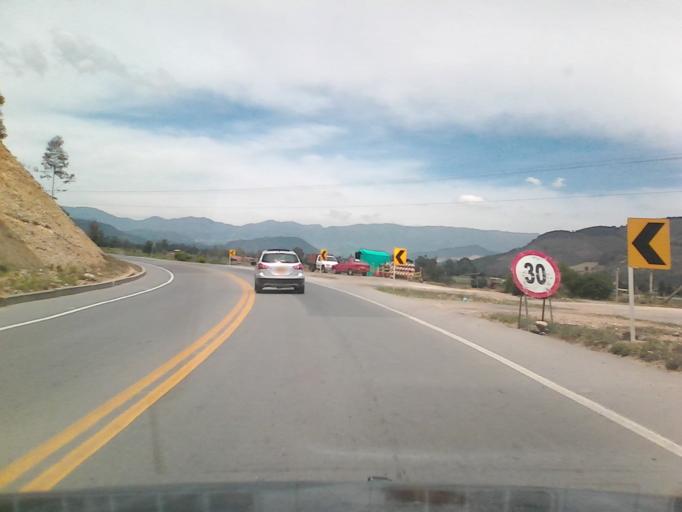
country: CO
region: Boyaca
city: Sogamoso
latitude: 5.7316
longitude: -72.9540
